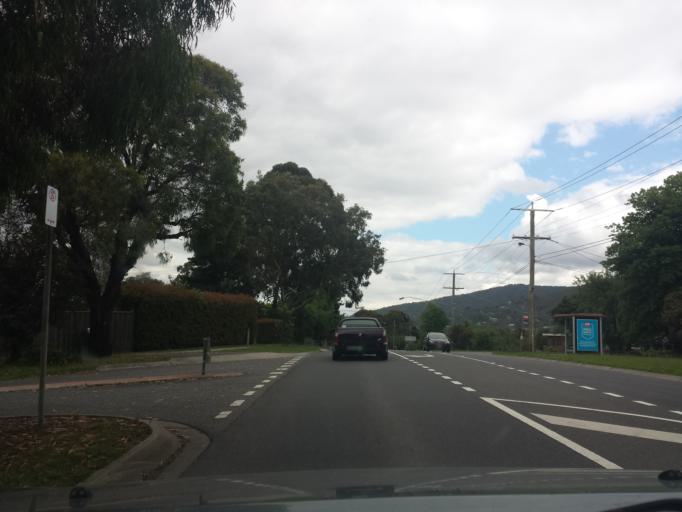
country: AU
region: Victoria
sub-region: Knox
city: Ferntree Gully
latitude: -37.8991
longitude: 145.2944
